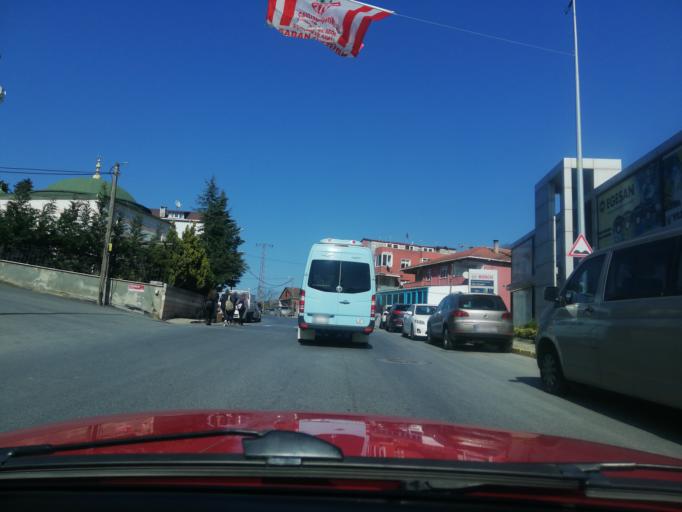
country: TR
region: Istanbul
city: Umraniye
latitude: 41.0906
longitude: 29.1409
